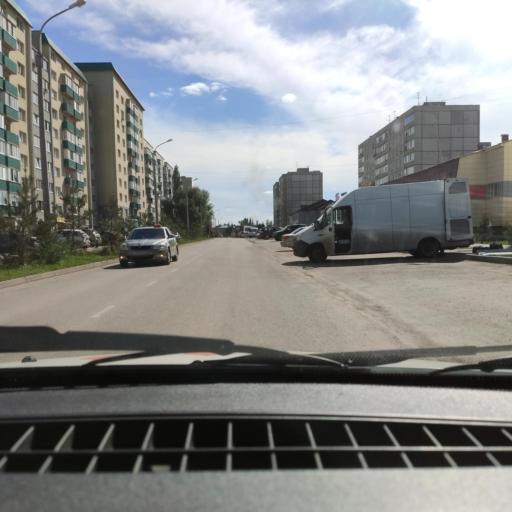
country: RU
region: Bashkortostan
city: Blagoveshchensk
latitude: 55.0510
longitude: 55.9615
